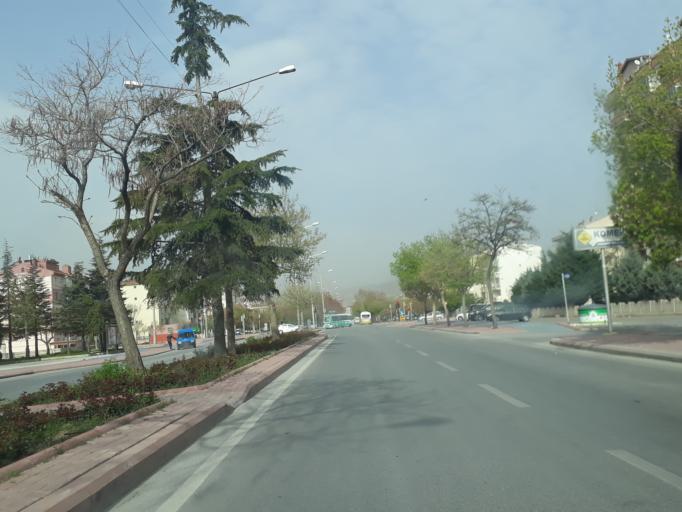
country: TR
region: Konya
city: Selcuklu
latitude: 37.9372
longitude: 32.5003
